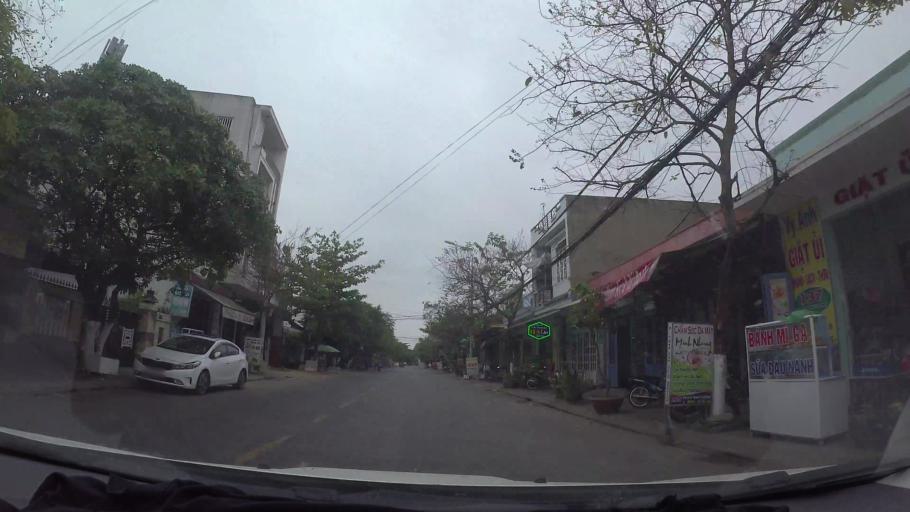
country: VN
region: Da Nang
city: Lien Chieu
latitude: 16.0647
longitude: 108.1511
